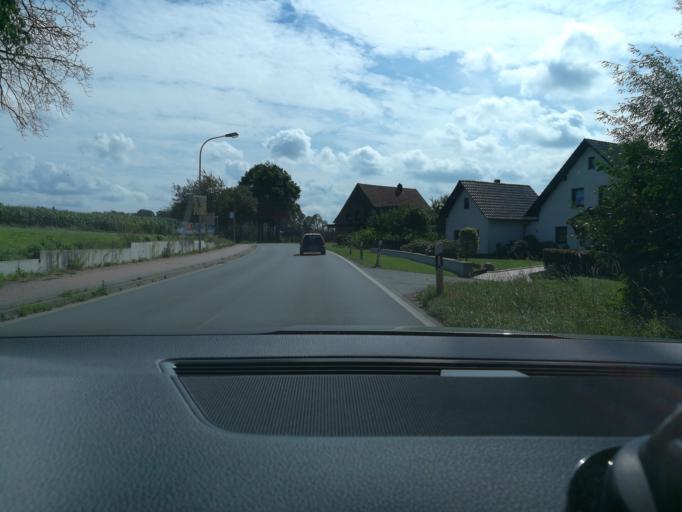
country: DE
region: North Rhine-Westphalia
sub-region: Regierungsbezirk Detmold
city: Huellhorst
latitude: 52.2808
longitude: 8.6957
